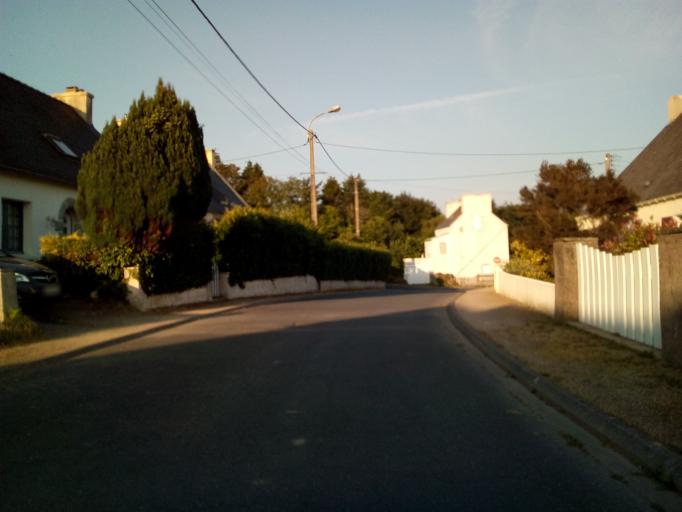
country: FR
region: Brittany
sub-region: Departement du Finistere
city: Landivisiau
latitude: 48.4987
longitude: -4.0796
